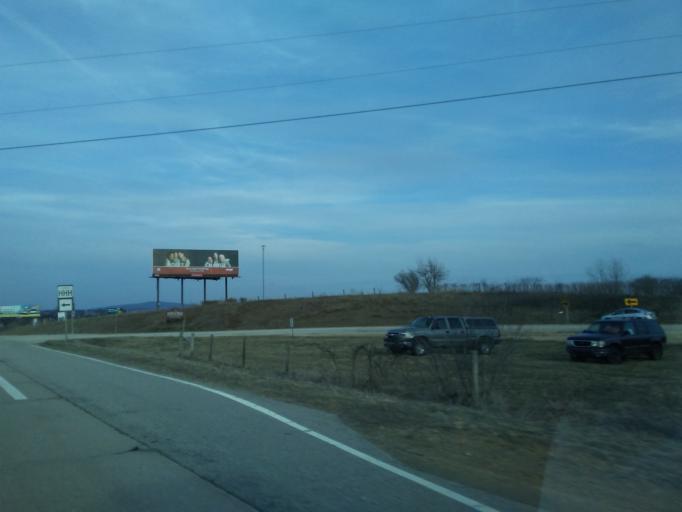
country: US
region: Wisconsin
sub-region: Iowa County
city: Barneveld
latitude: 42.9926
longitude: -90.0015
